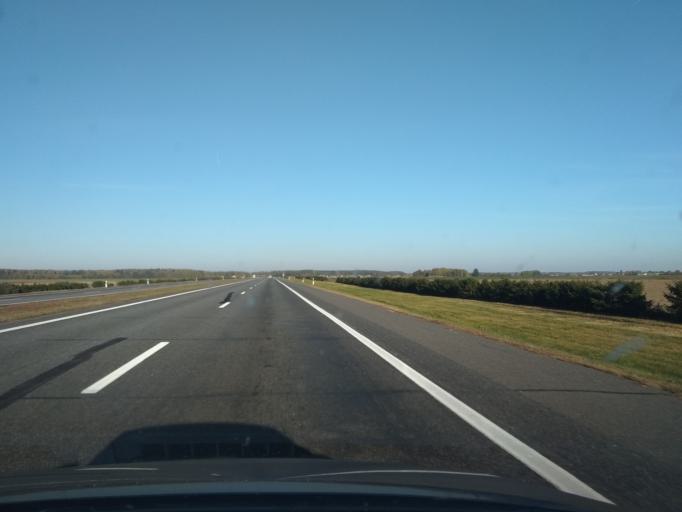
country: BY
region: Brest
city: Ivatsevichy
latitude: 52.6665
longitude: 25.2943
